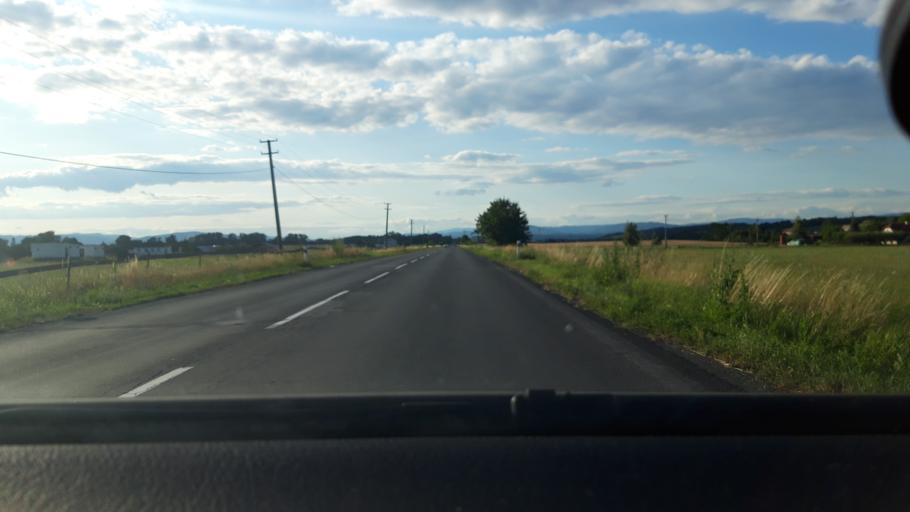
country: SK
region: Banskobystricky
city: Lucenec
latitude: 48.3119
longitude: 19.7077
